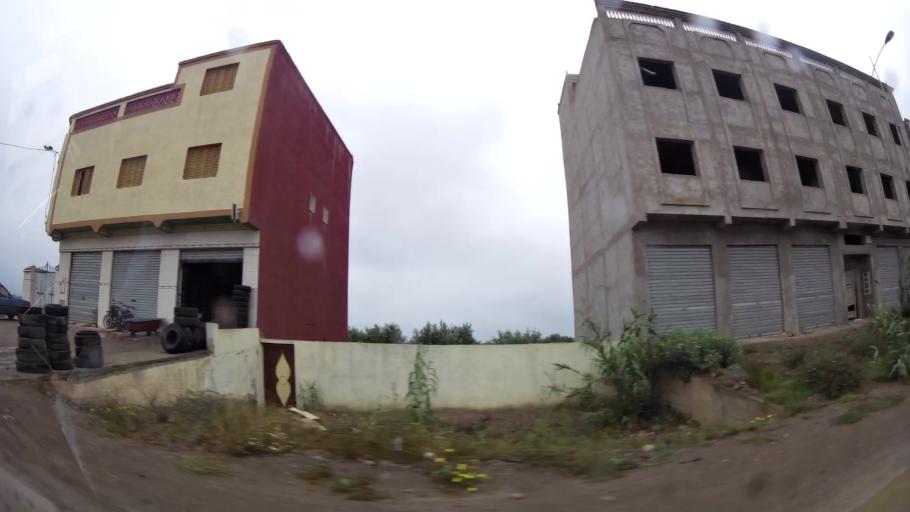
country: MA
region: Taza-Al Hoceima-Taounate
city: Imzourene
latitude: 35.1540
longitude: -3.8280
